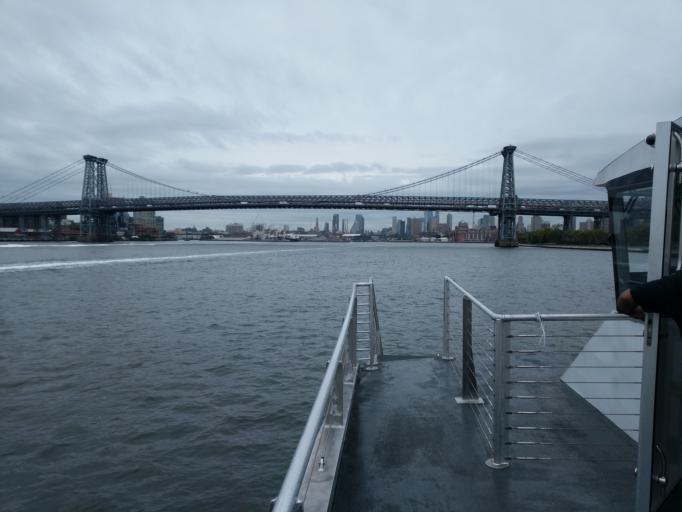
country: US
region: New York
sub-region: Queens County
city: Long Island City
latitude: 40.7189
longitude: -73.9716
